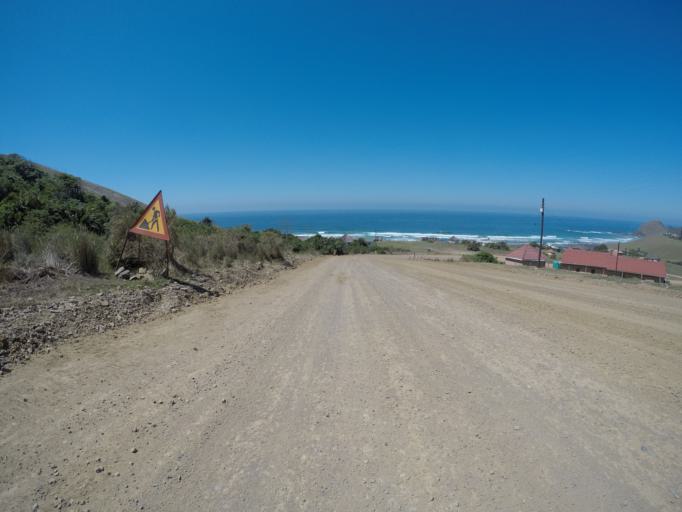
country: ZA
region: Eastern Cape
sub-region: OR Tambo District Municipality
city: Libode
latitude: -32.0260
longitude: 29.1160
